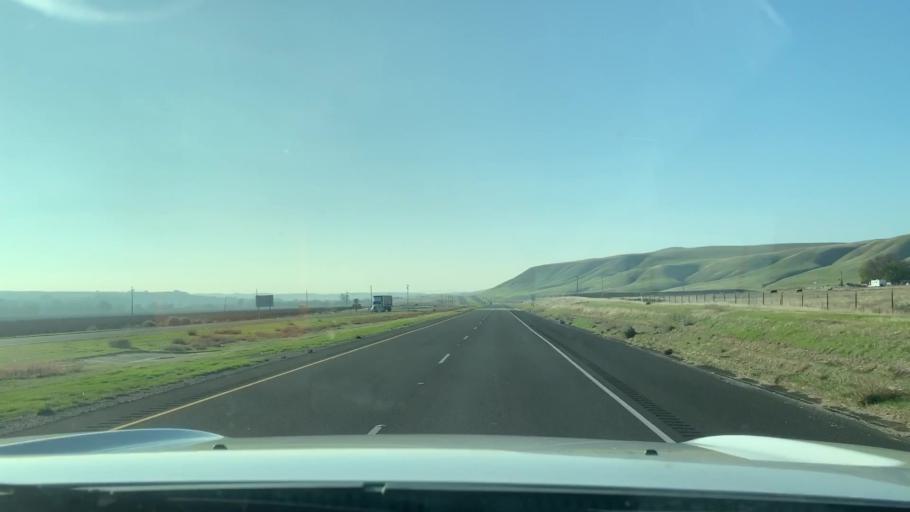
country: US
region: California
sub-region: San Luis Obispo County
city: Shandon
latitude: 35.6617
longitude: -120.4252
